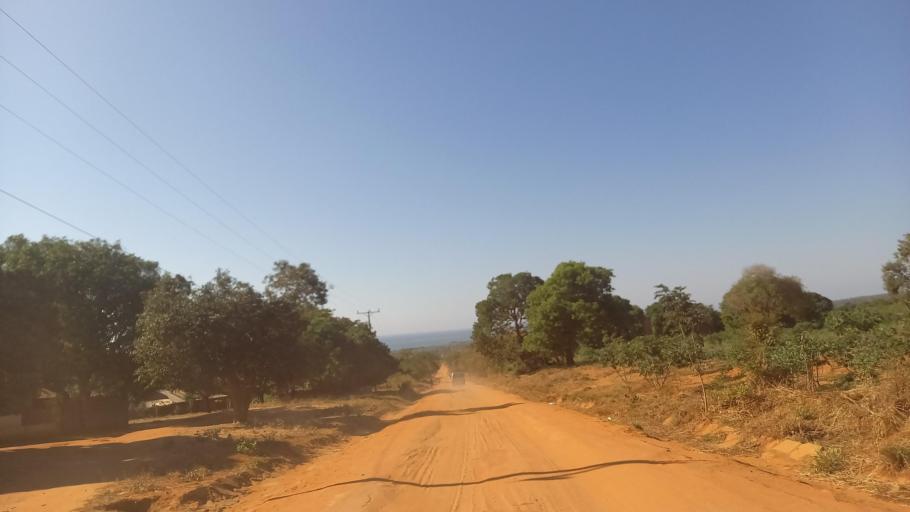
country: MZ
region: Cabo Delgado
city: Pemba
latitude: -13.0933
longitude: 40.5320
